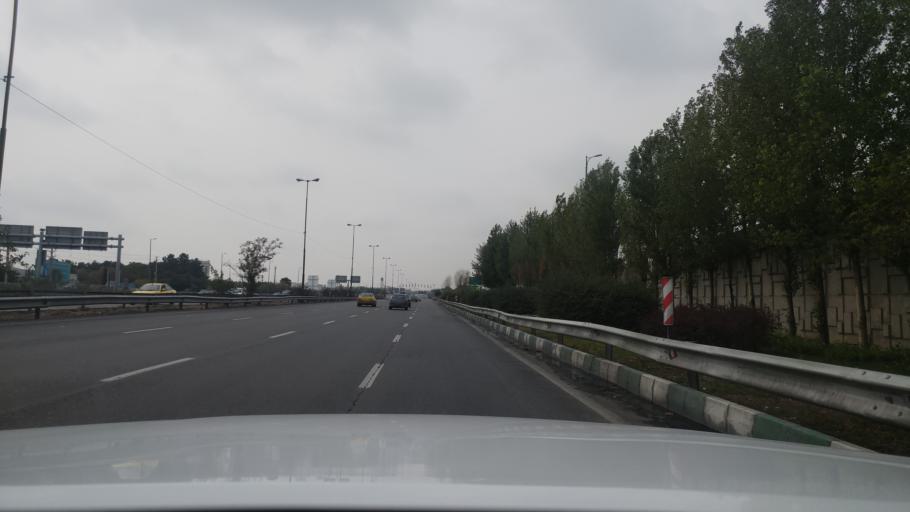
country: IR
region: Tehran
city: Tehran
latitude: 35.7167
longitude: 51.2961
